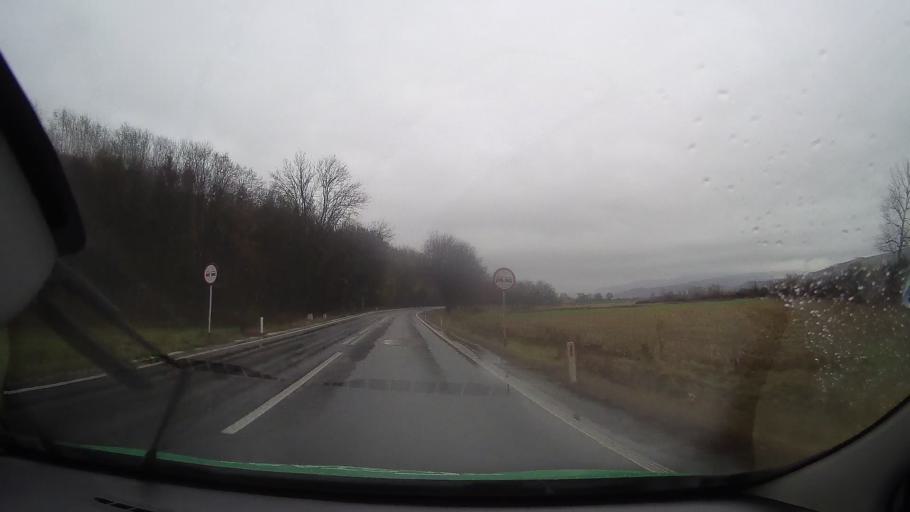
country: RO
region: Mures
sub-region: Comuna Brancovenesti
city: Valenii de Mures
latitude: 46.8785
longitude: 24.7778
